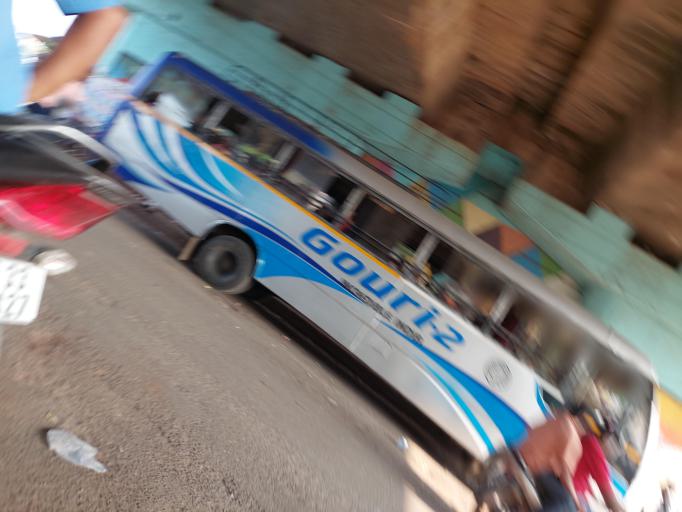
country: IN
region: Odisha
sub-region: Khordha
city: Bhubaneshwar
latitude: 20.2716
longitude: 85.7938
